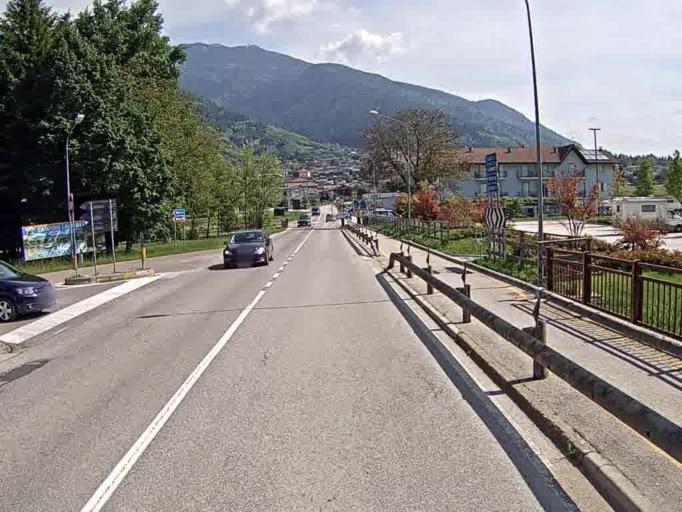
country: IT
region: Trentino-Alto Adige
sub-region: Provincia di Trento
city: Levico Terme
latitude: 46.0054
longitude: 11.2908
